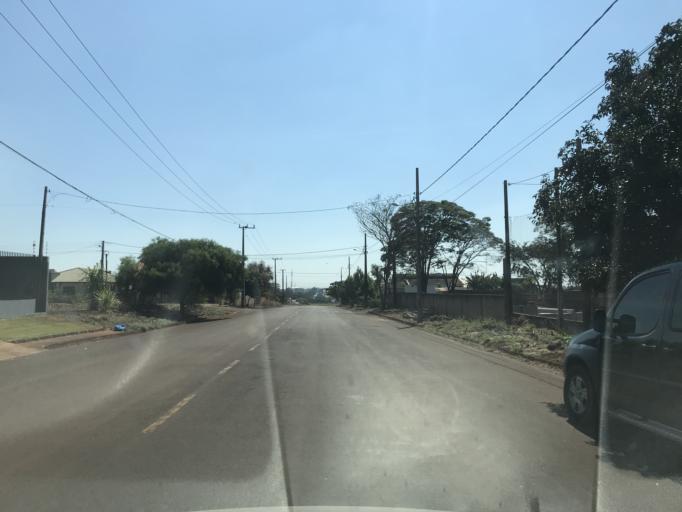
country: BR
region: Parana
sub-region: Palotina
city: Palotina
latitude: -24.2965
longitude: -53.8319
